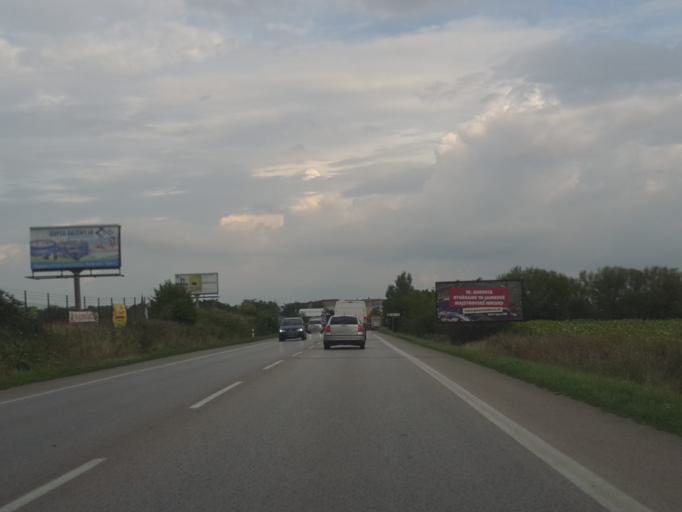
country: SK
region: Bratislavsky
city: Senec
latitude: 48.2255
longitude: 17.3817
